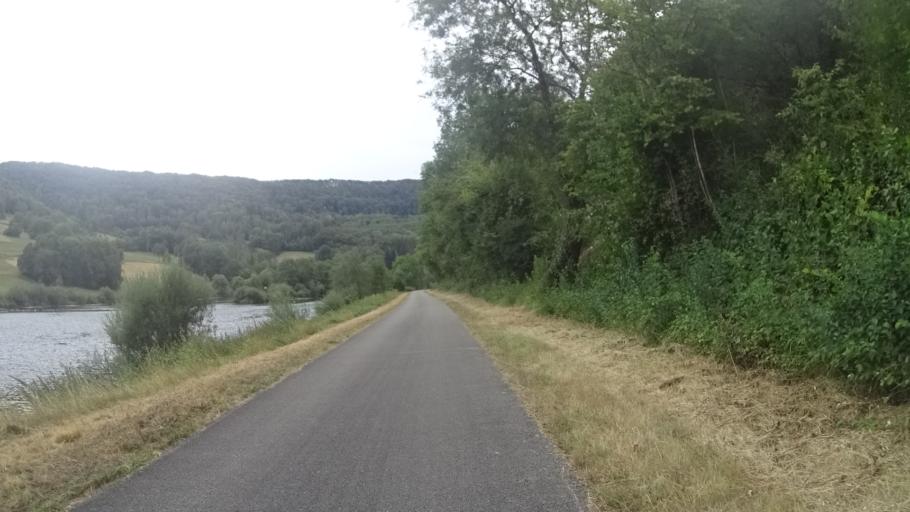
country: FR
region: Franche-Comte
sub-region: Departement du Doubs
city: Baume-les-Dames
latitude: 47.3355
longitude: 6.3141
